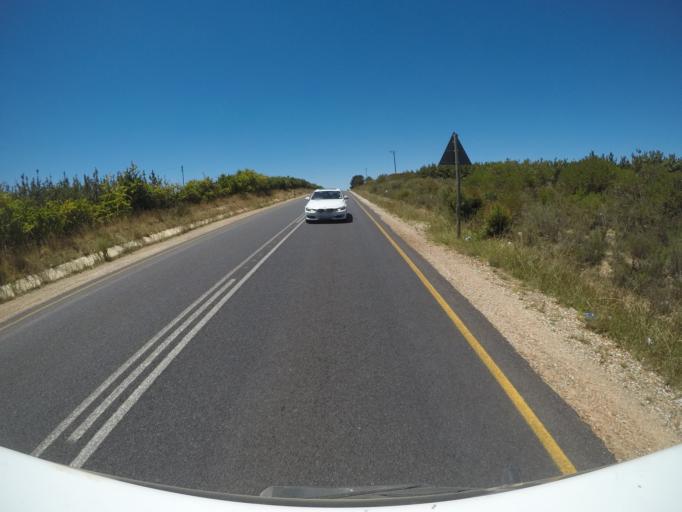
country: ZA
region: Western Cape
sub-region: Overberg District Municipality
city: Grabouw
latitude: -34.0676
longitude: 19.1169
